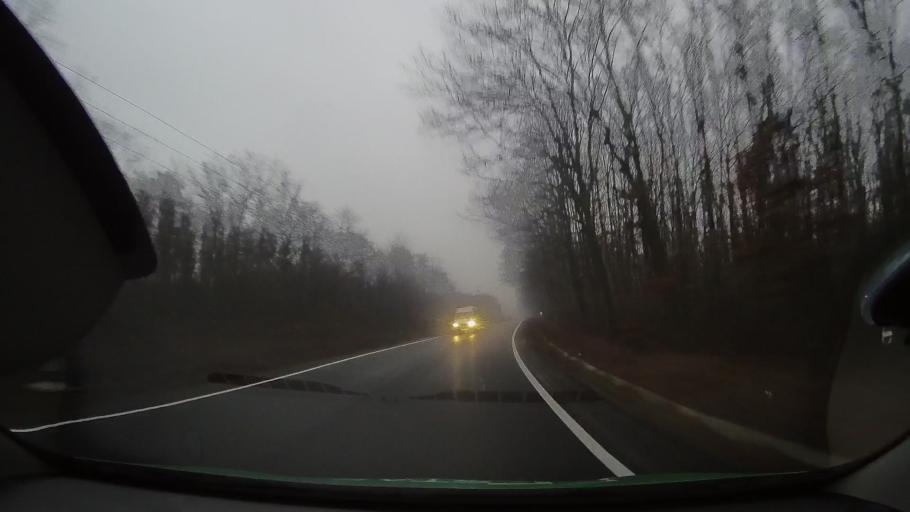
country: RO
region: Bihor
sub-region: Comuna Olcea
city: Olcea
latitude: 46.6997
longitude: 21.9646
